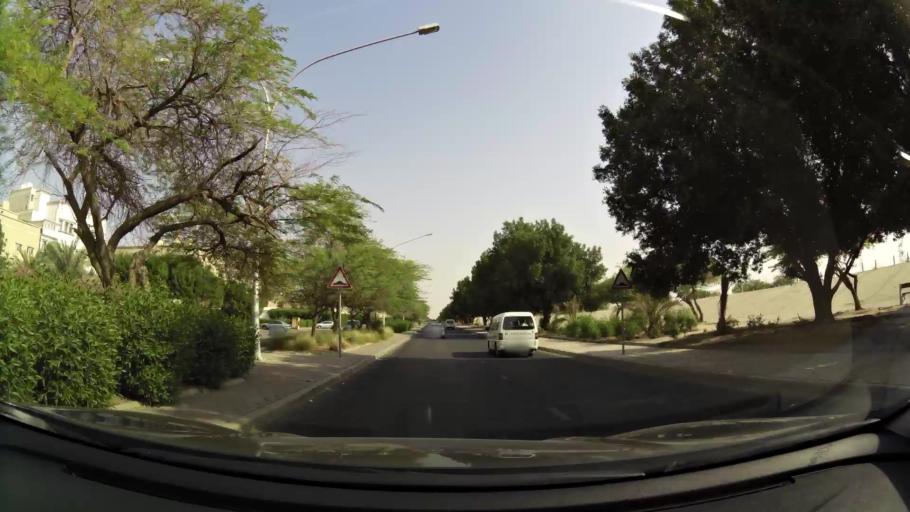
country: KW
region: Muhafazat al Jahra'
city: Al Jahra'
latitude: 29.3178
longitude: 47.6719
